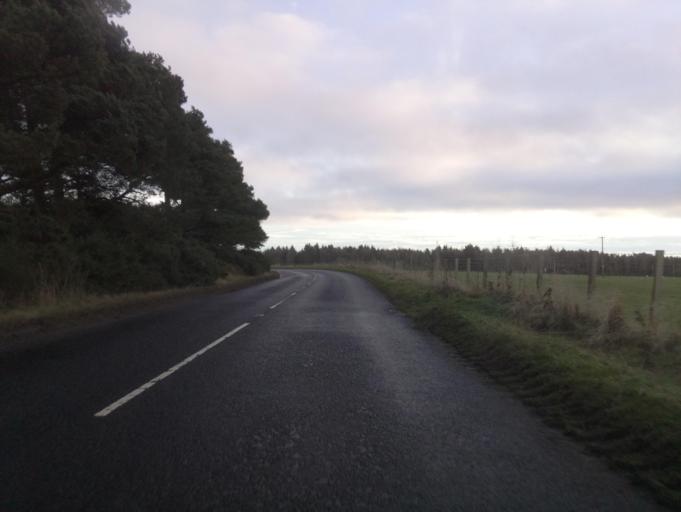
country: GB
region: Scotland
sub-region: Angus
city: Letham
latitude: 56.5544
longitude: -2.7620
